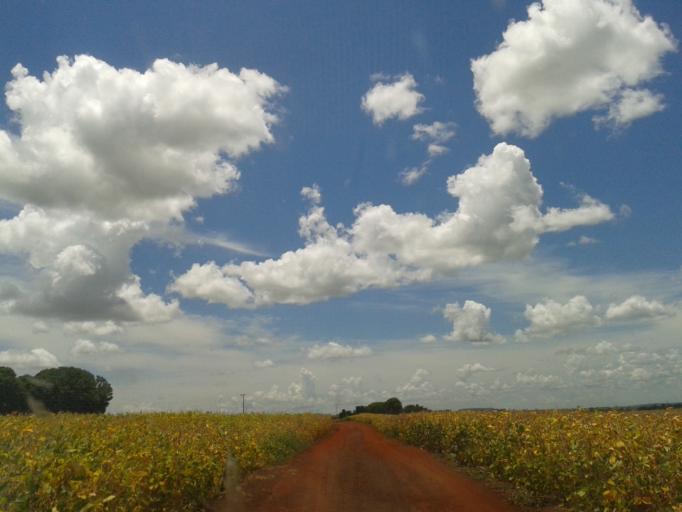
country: BR
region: Minas Gerais
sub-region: Capinopolis
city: Capinopolis
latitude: -18.7649
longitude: -49.7932
